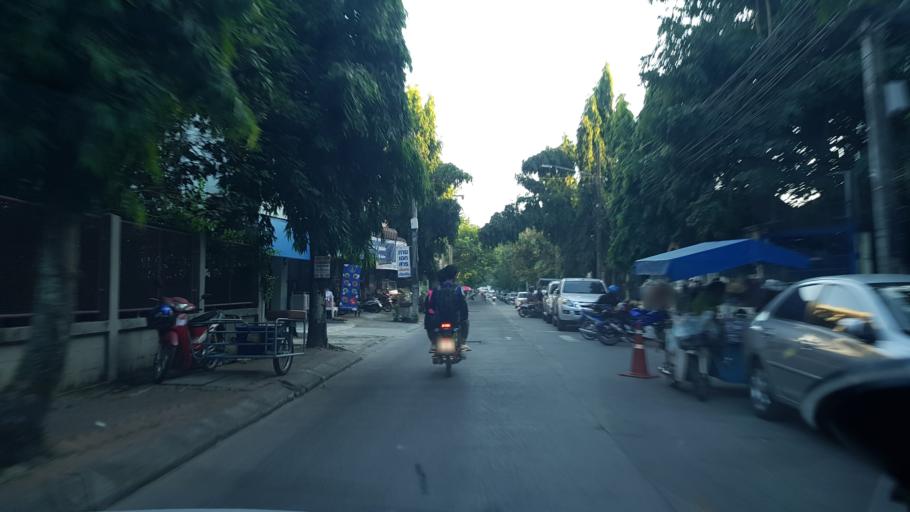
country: TH
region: Chiang Rai
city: Chiang Rai
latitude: 19.9107
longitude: 99.8349
